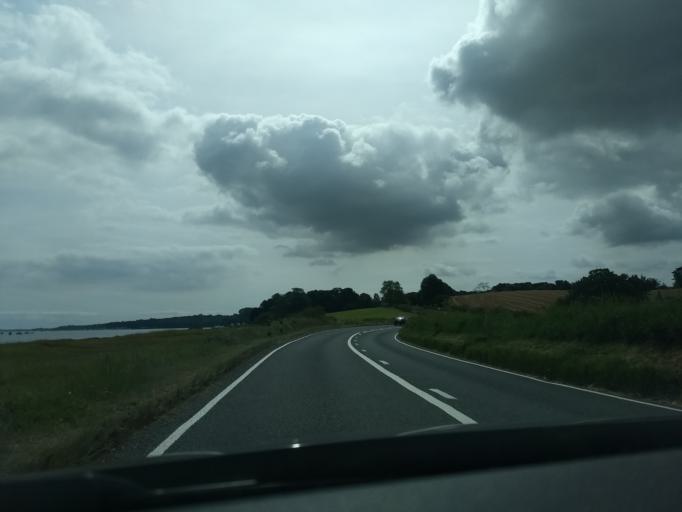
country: GB
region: England
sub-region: Suffolk
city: Ipswich
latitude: 52.0194
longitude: 1.1657
